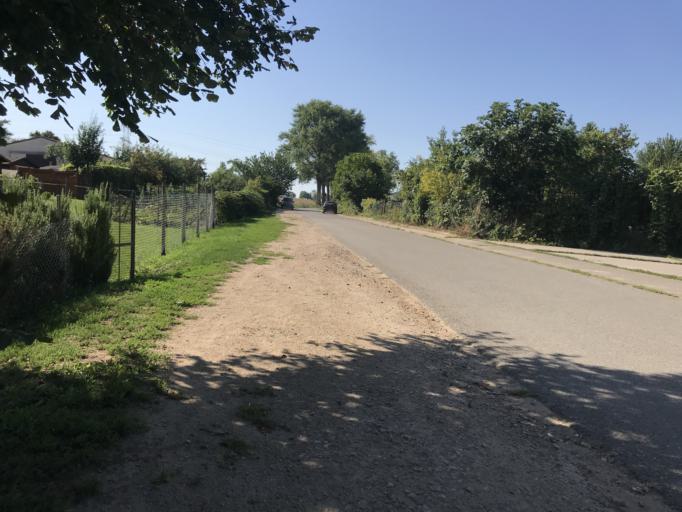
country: DE
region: Rheinland-Pfalz
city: Mainz
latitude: 49.9542
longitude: 8.2811
